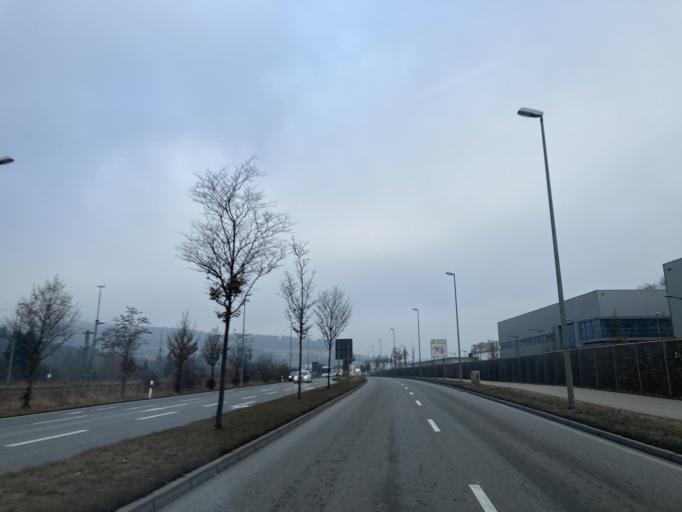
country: DE
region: Baden-Wuerttemberg
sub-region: Freiburg Region
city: Tuttlingen
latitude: 47.9757
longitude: 8.7947
